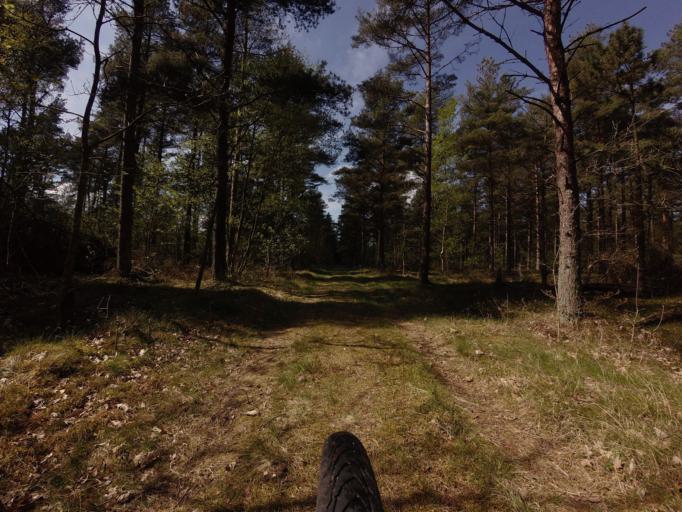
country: DK
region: North Denmark
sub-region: Jammerbugt Kommune
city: Brovst
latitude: 57.1635
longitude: 9.5741
